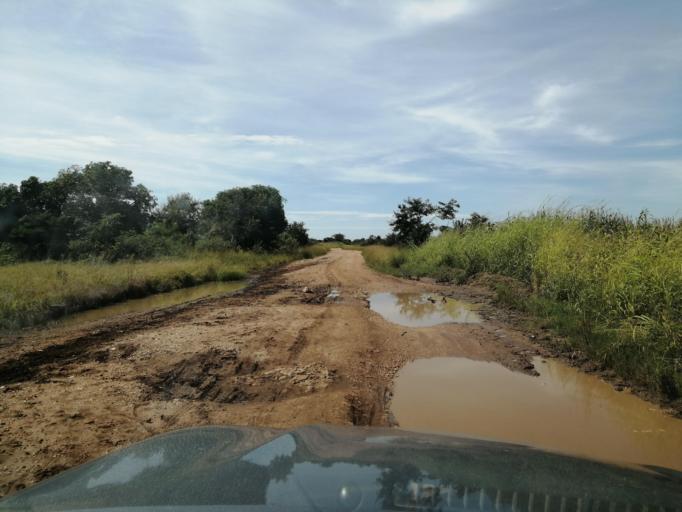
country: ZM
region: Central
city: Chibombo
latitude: -14.9883
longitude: 27.8114
